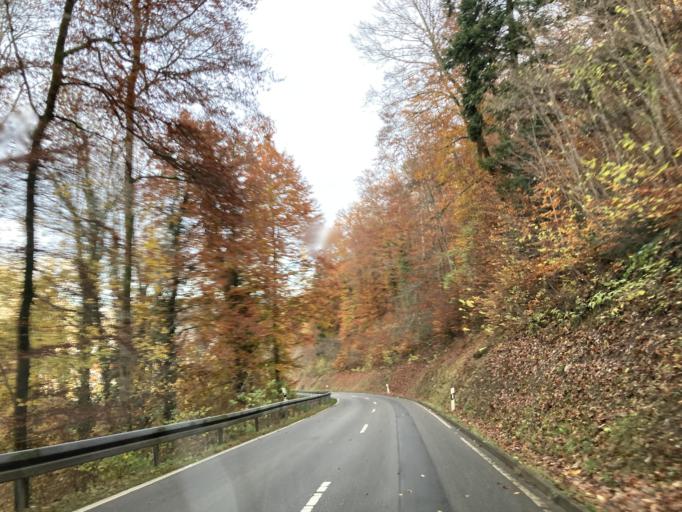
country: DE
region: Baden-Wuerttemberg
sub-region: Karlsruhe Region
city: Empfingen
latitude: 48.4161
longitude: 8.7510
